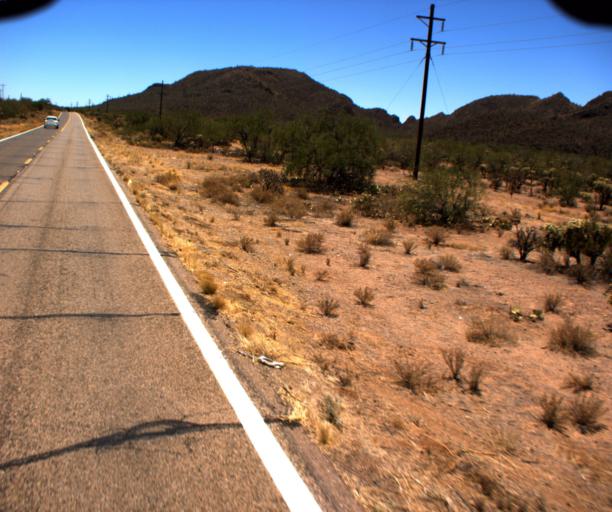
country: US
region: Arizona
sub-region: Pima County
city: Sells
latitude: 31.9632
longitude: -111.9528
